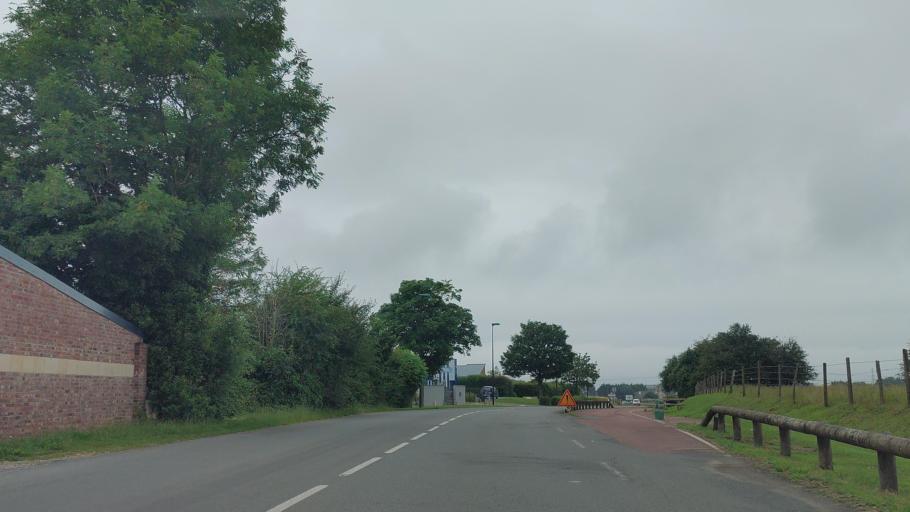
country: FR
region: Picardie
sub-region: Departement de la Somme
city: Ault
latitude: 50.0911
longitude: 1.4710
